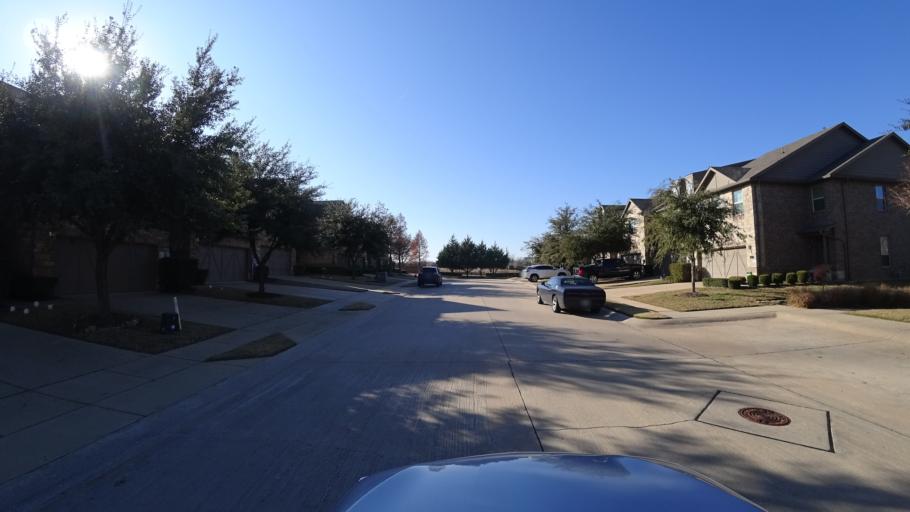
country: US
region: Texas
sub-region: Denton County
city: Lewisville
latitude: 33.0072
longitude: -96.9817
